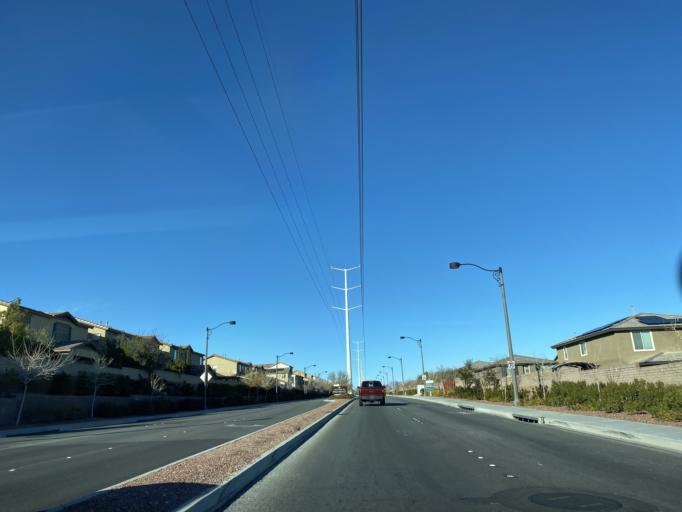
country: US
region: Nevada
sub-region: Clark County
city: Summerlin South
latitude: 36.2775
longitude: -115.3289
